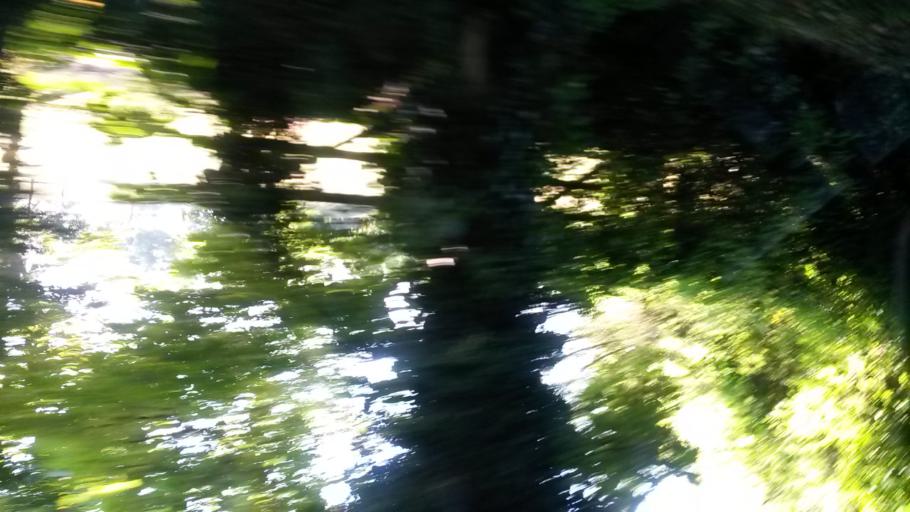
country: IE
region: Leinster
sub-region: Dublin City
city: Finglas
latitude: 53.4595
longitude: -6.3244
